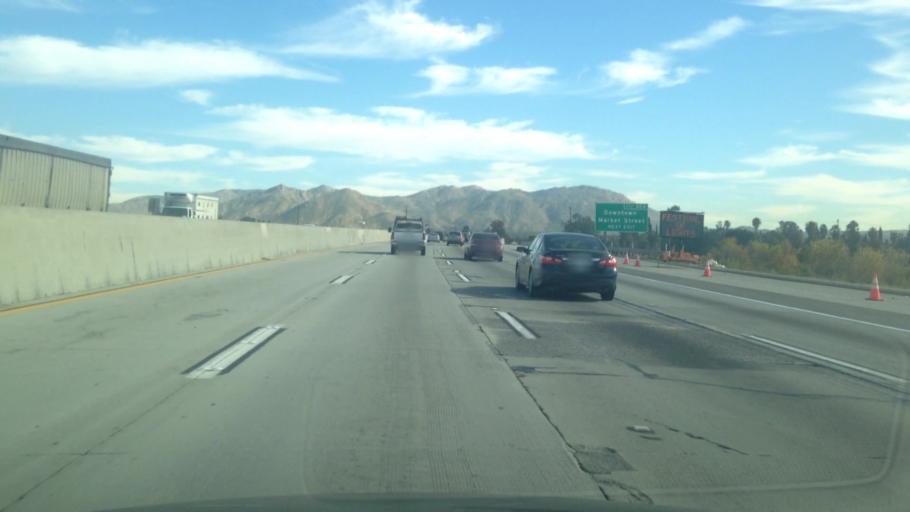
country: US
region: California
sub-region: Riverside County
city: Rubidoux
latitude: 34.0045
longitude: -117.3852
